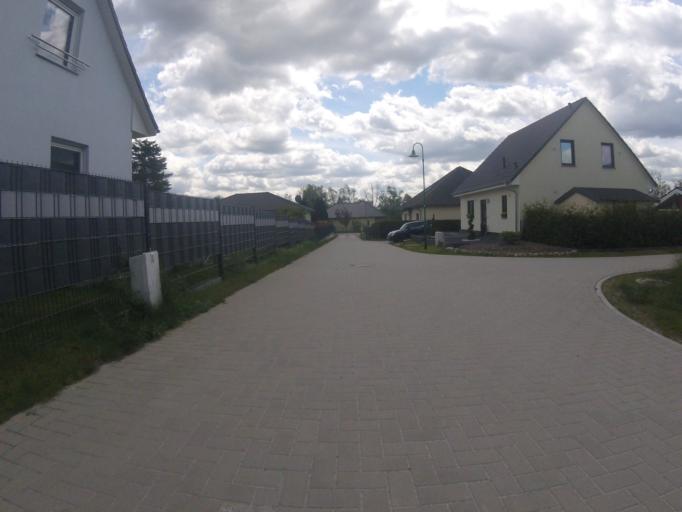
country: DE
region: Brandenburg
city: Bestensee
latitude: 52.2620
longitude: 13.6238
